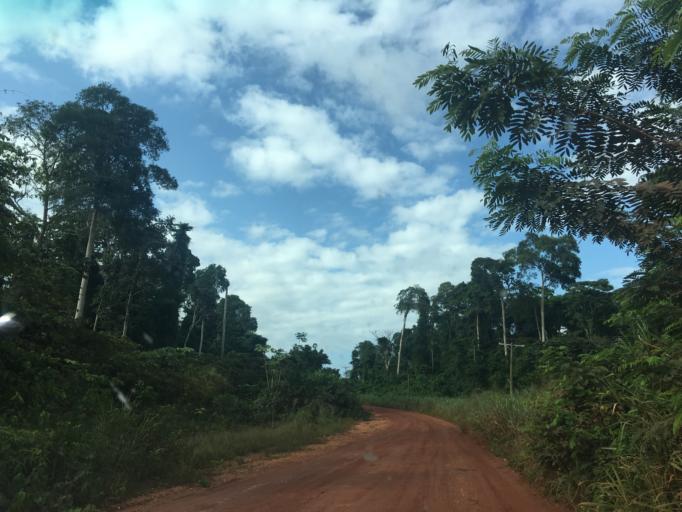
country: GH
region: Western
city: Wassa-Akropong
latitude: 5.9619
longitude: -2.4253
